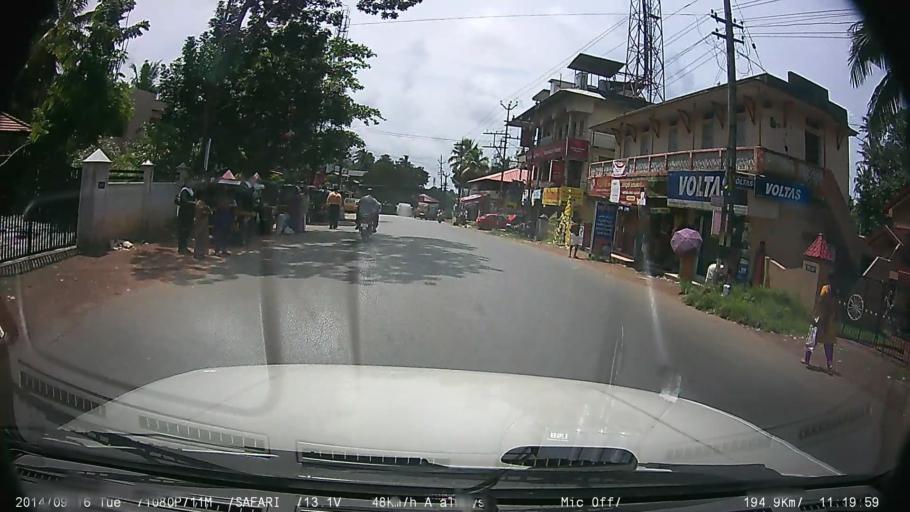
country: IN
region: Kerala
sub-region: Kottayam
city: Changanacheri
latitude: 9.4877
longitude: 76.5249
